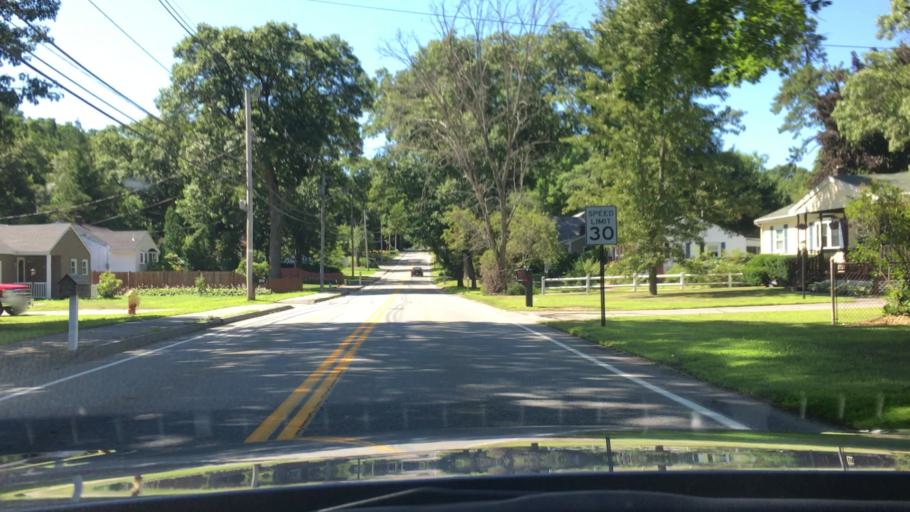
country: US
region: Massachusetts
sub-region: Middlesex County
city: Billerica
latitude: 42.5739
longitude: -71.2620
